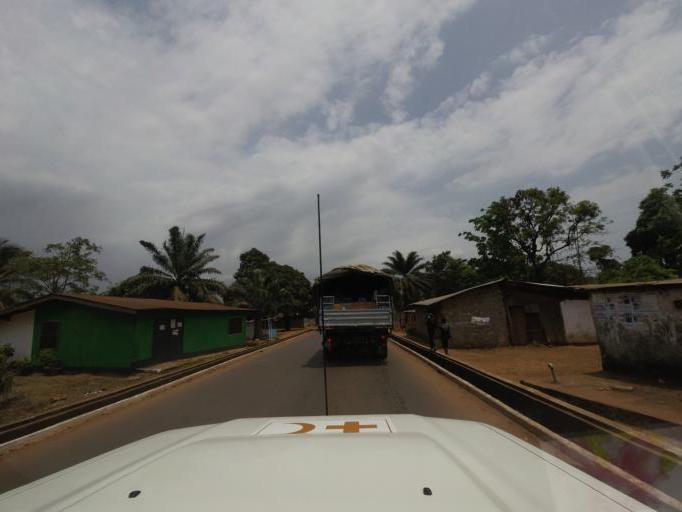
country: LR
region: Montserrado
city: Monrovia
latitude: 6.3064
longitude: -10.6931
